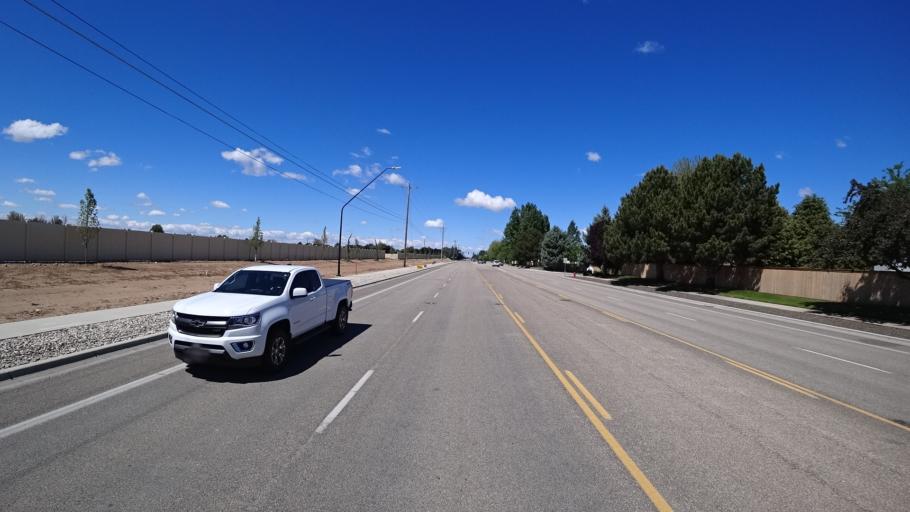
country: US
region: Idaho
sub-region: Ada County
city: Meridian
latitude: 43.6337
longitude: -116.3711
